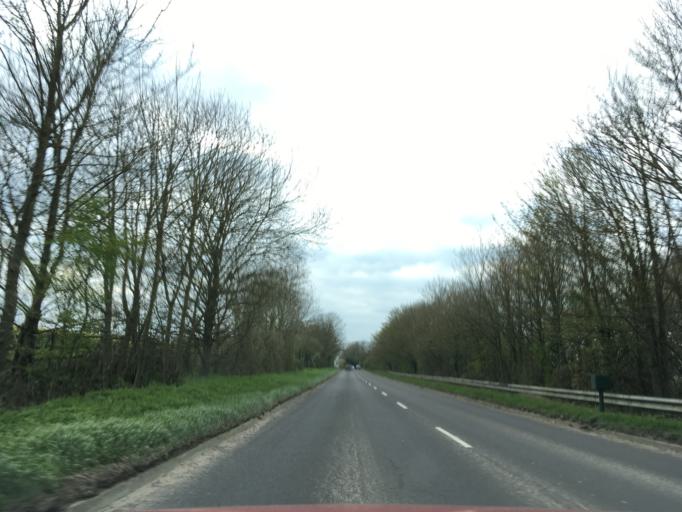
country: GB
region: England
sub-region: Oxfordshire
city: Witney
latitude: 51.7957
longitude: -1.5377
